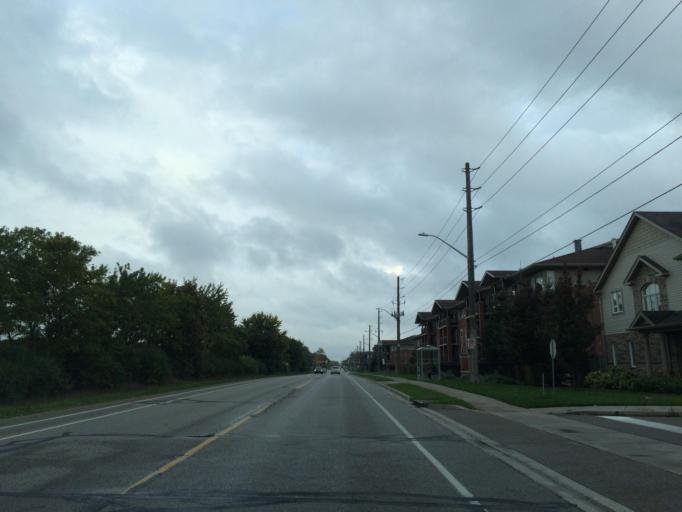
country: CA
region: Ontario
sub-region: Wellington County
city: Guelph
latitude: 43.5179
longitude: -80.1773
